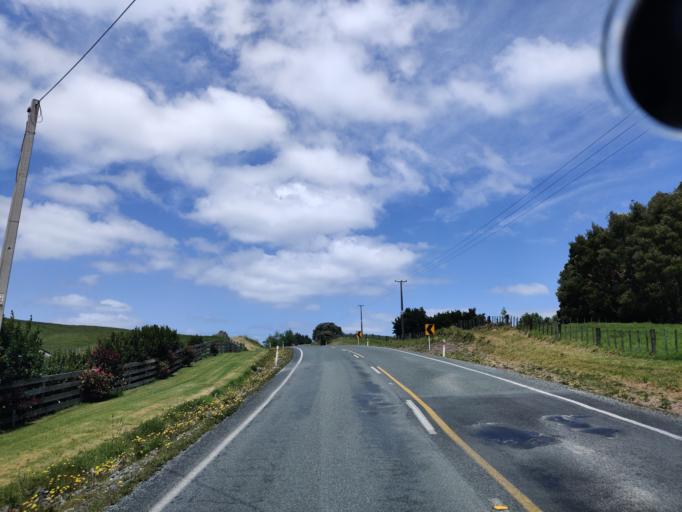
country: NZ
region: Auckland
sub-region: Auckland
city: Wellsford
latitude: -36.3968
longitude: 174.4452
